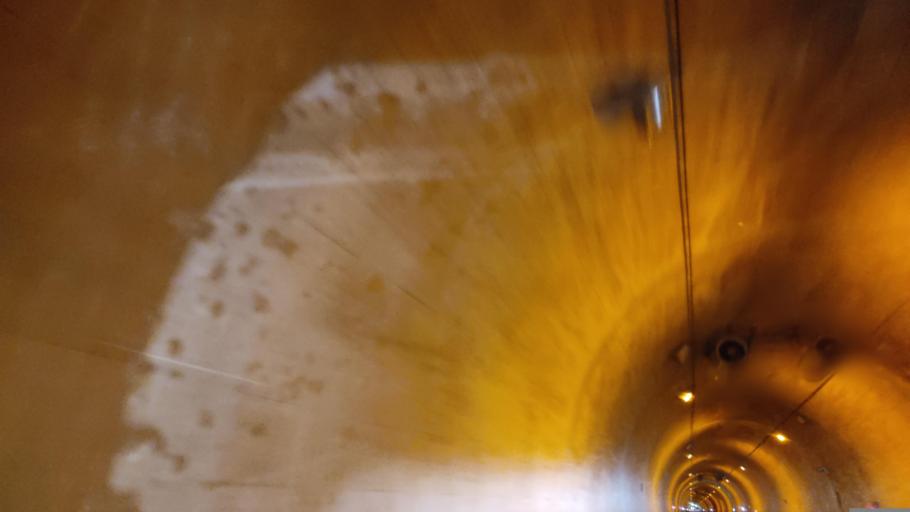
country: JP
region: Iwate
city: Shizukuishi
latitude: 39.6318
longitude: 141.0544
